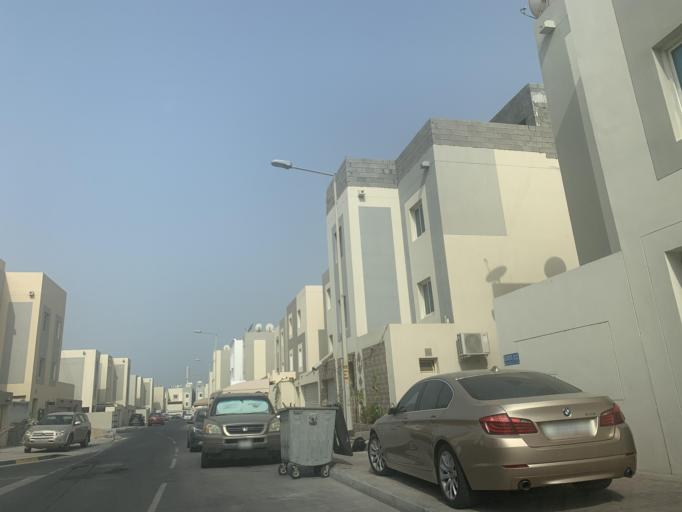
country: BH
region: Manama
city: Jidd Hafs
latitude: 26.2322
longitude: 50.4473
